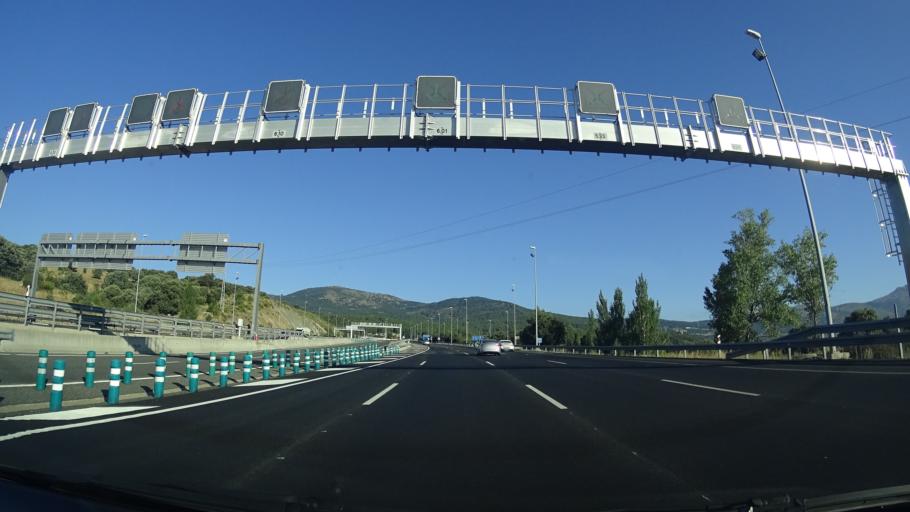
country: ES
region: Madrid
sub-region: Provincia de Madrid
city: Guadarrama
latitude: 40.6683
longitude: -4.1037
